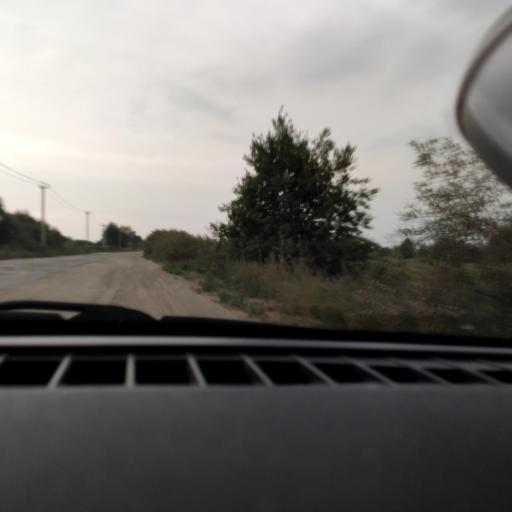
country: RU
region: Perm
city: Kondratovo
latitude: 58.0005
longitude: 56.0117
